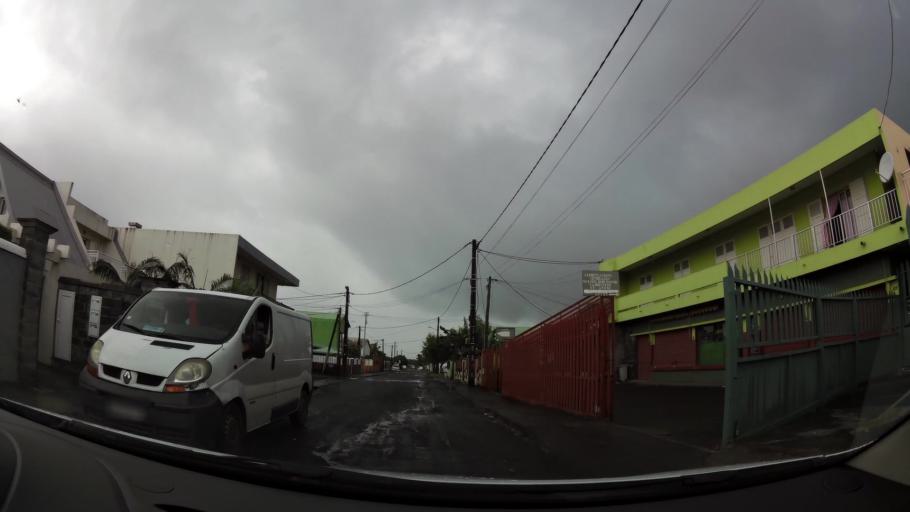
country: RE
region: Reunion
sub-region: Reunion
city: Saint-Andre
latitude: -20.9293
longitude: 55.6449
